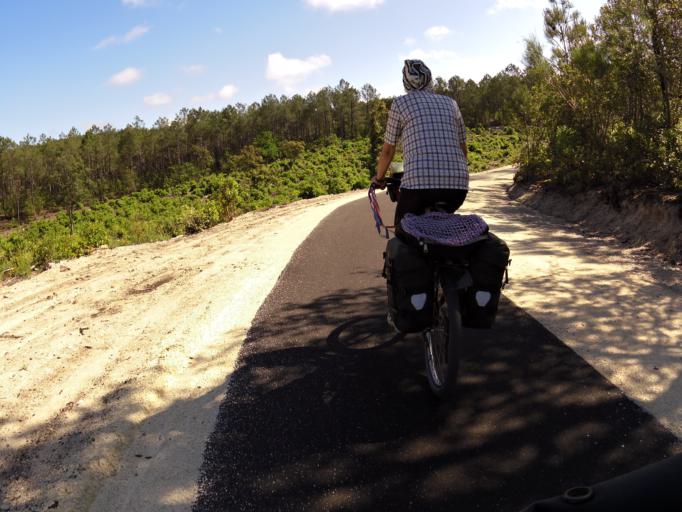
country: FR
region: Aquitaine
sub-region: Departement de la Gironde
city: Lacanau
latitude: 45.0311
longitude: -1.1658
